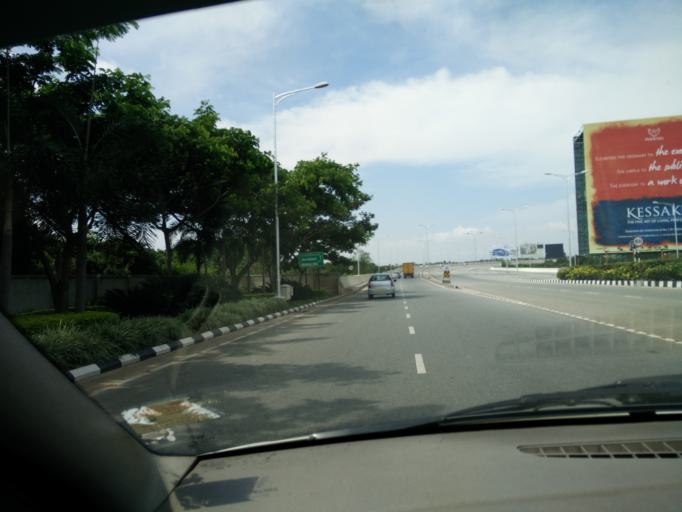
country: IN
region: Karnataka
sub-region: Bangalore Rural
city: Devanhalli
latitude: 13.1981
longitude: 77.6674
